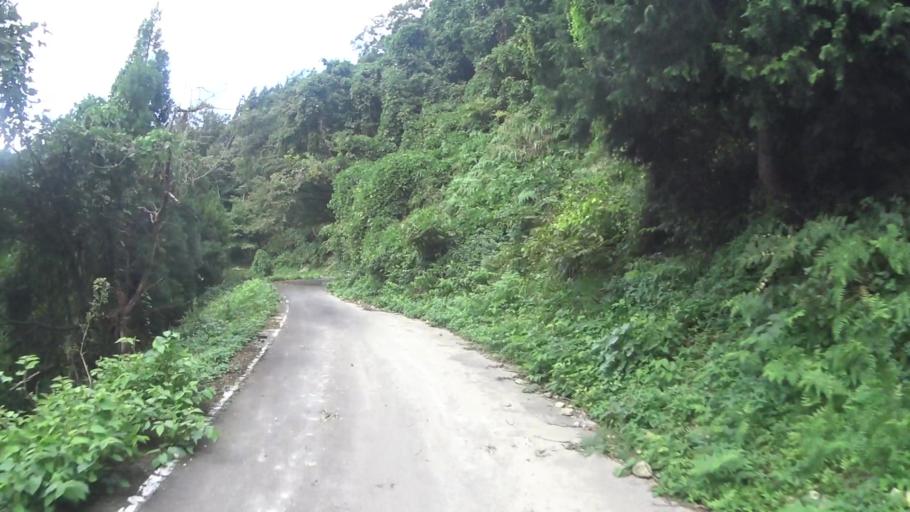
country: JP
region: Kyoto
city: Miyazu
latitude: 35.7412
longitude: 135.1982
